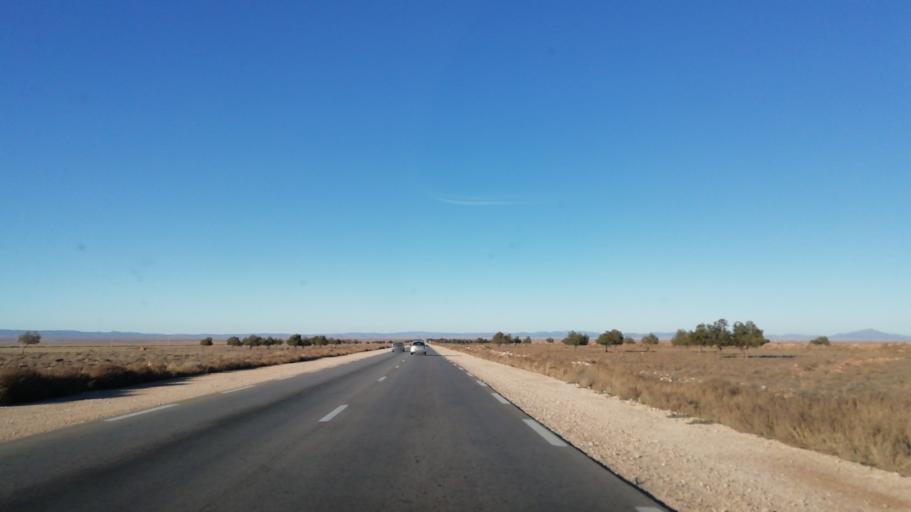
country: DZ
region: Tlemcen
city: Sebdou
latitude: 34.3275
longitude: -1.2639
